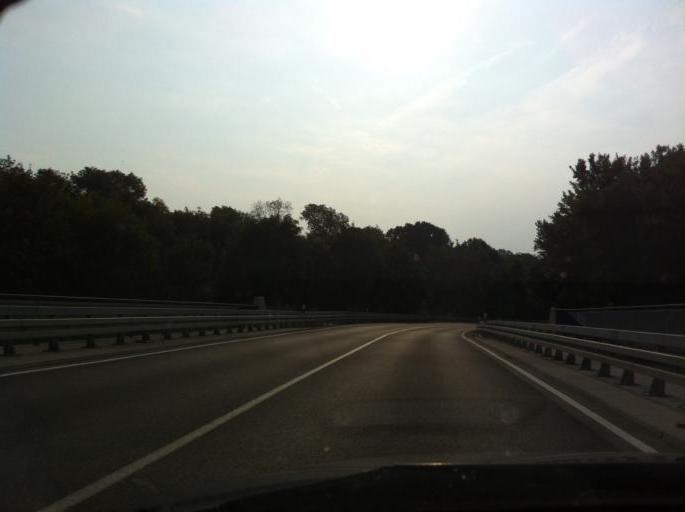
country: DE
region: Saxony
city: Markkleeberg
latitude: 51.2990
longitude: 12.3425
